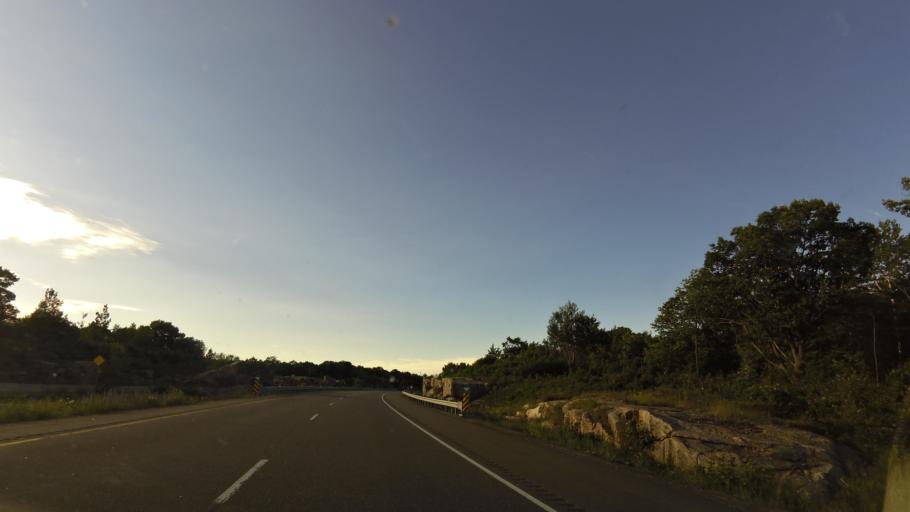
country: CA
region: Ontario
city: Midland
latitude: 44.8709
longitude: -79.7478
